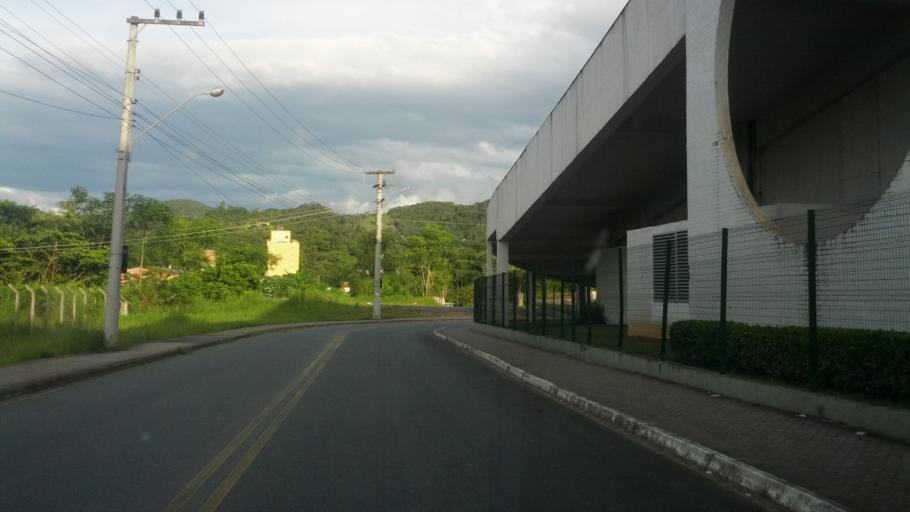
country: BR
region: Santa Catarina
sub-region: Blumenau
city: Blumenau
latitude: -26.8855
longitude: -49.0682
